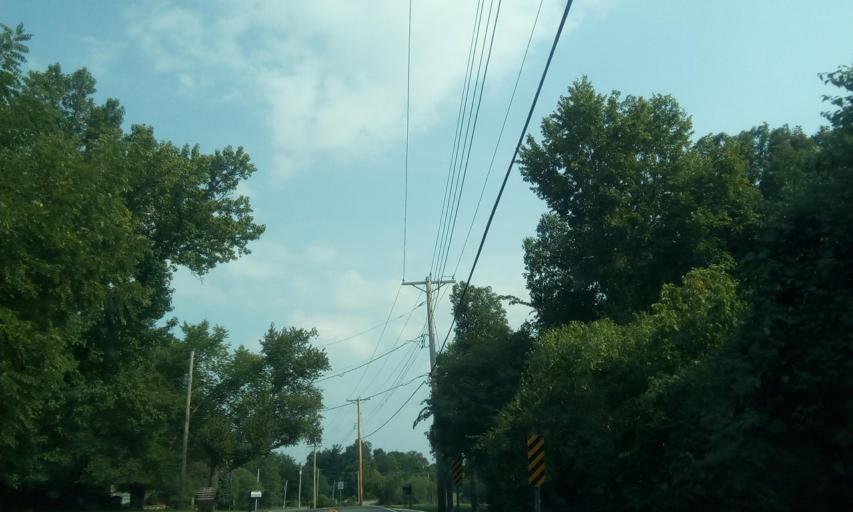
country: US
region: Missouri
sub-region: Saint Louis County
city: Town and Country
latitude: 38.6044
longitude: -90.4843
